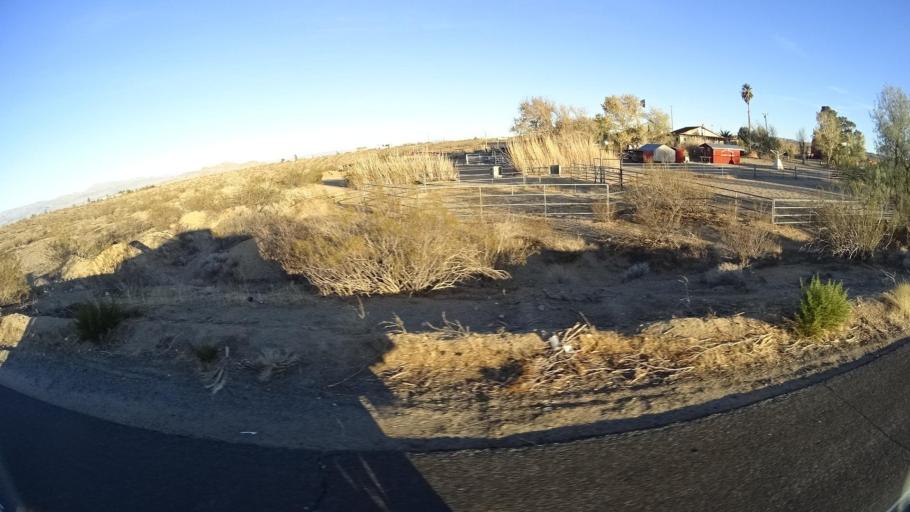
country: US
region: California
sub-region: Kern County
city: China Lake Acres
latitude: 35.6097
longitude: -117.7231
